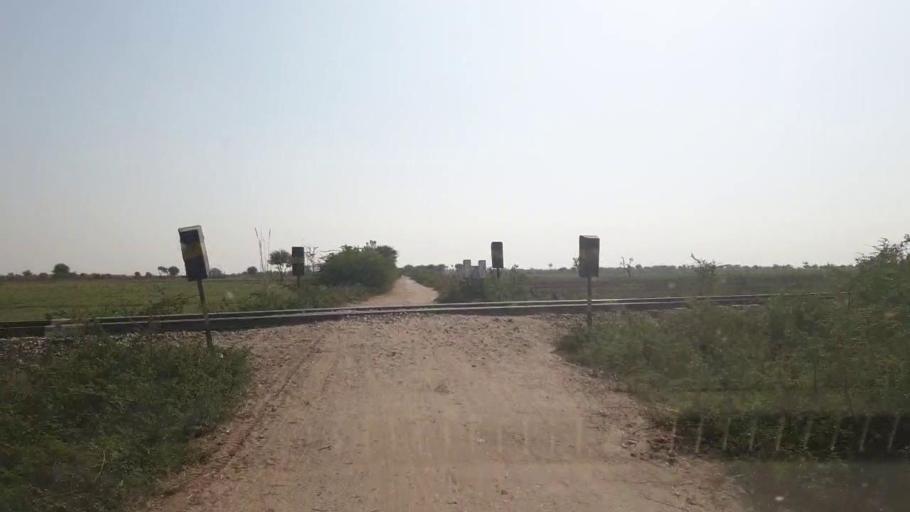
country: PK
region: Sindh
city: Dhoro Naro
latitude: 25.5019
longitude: 69.5865
